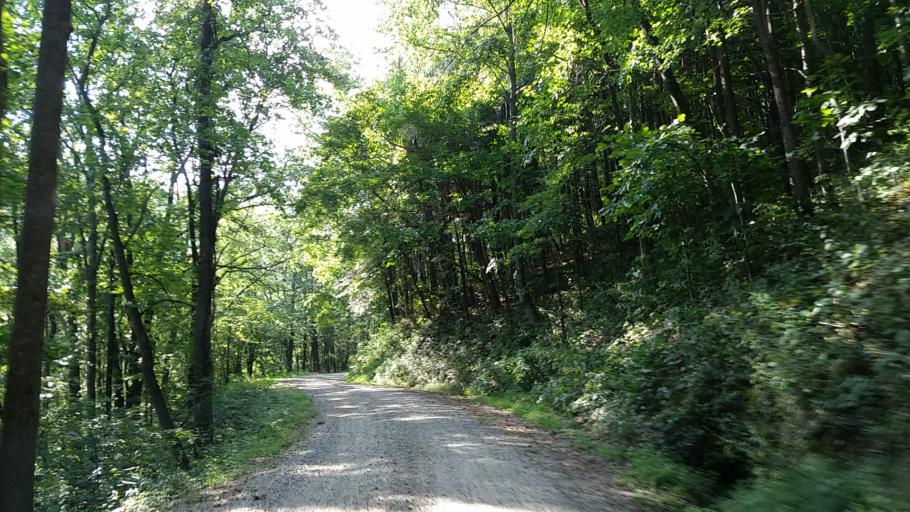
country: US
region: Georgia
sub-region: Lumpkin County
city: Dahlonega
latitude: 34.6401
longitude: -84.0396
